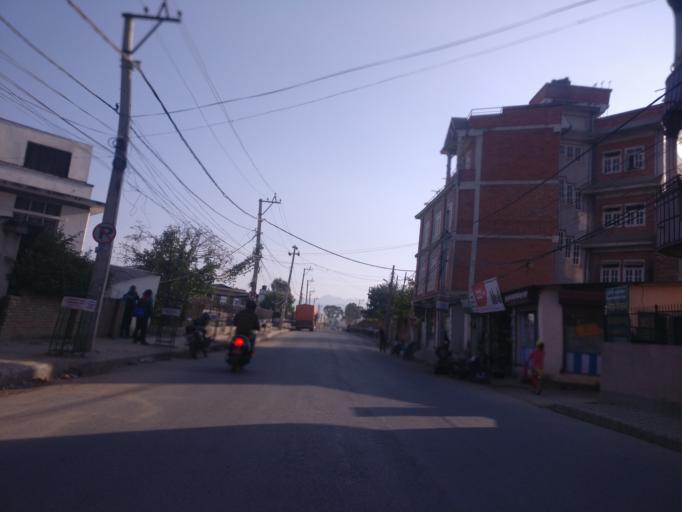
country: NP
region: Central Region
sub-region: Bagmati Zone
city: Patan
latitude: 27.6562
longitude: 85.3259
